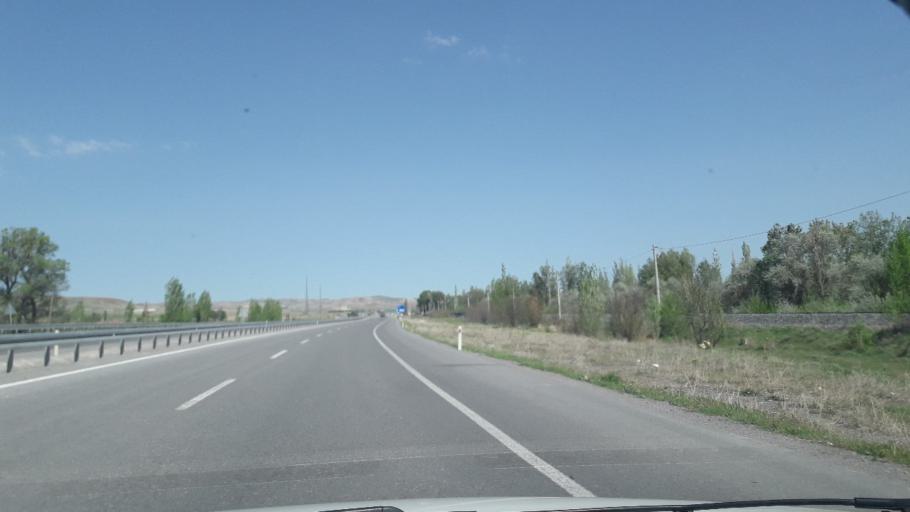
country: TR
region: Sivas
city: Ulas
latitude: 39.4383
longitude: 37.0406
